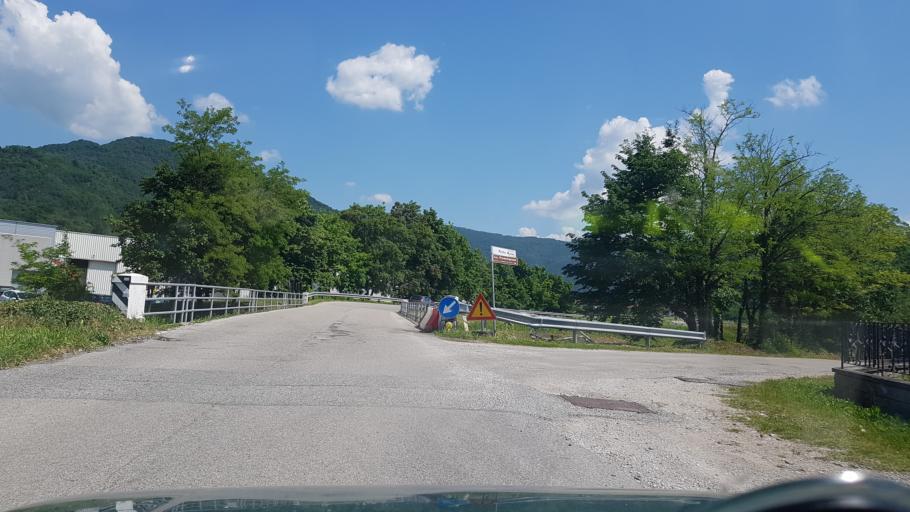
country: IT
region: Friuli Venezia Giulia
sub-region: Provincia di Udine
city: Torreano
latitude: 46.1153
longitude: 13.4143
